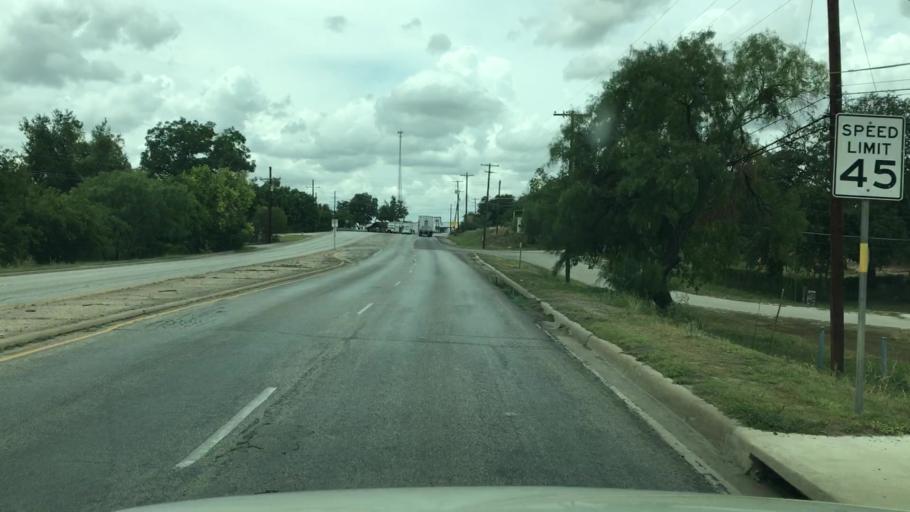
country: US
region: Texas
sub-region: McCulloch County
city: Brady
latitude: 31.1362
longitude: -99.3431
